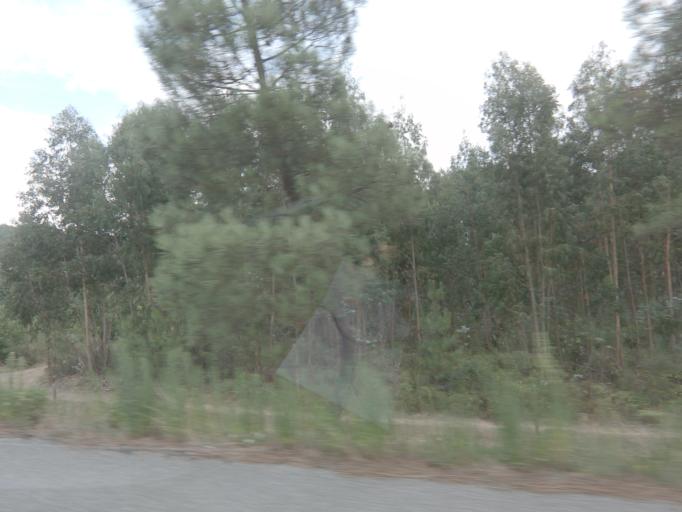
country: PT
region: Coimbra
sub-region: Penacova
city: Lorvao
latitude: 40.3062
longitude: -8.3426
